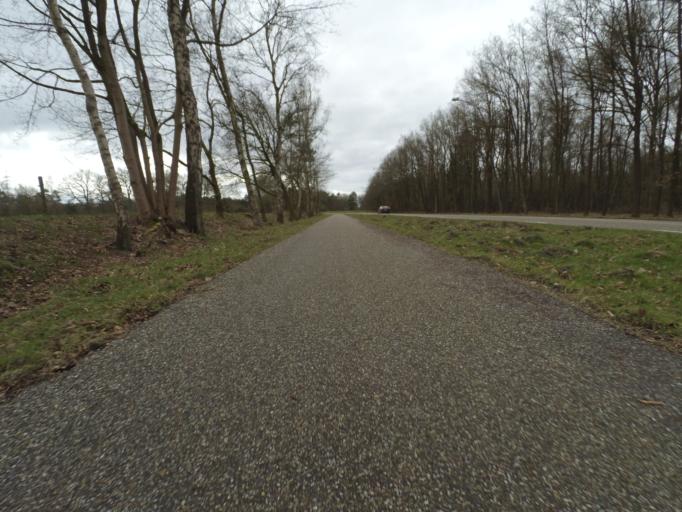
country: NL
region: Gelderland
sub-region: Gemeente Apeldoorn
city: Beekbergen
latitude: 52.1028
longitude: 5.9520
